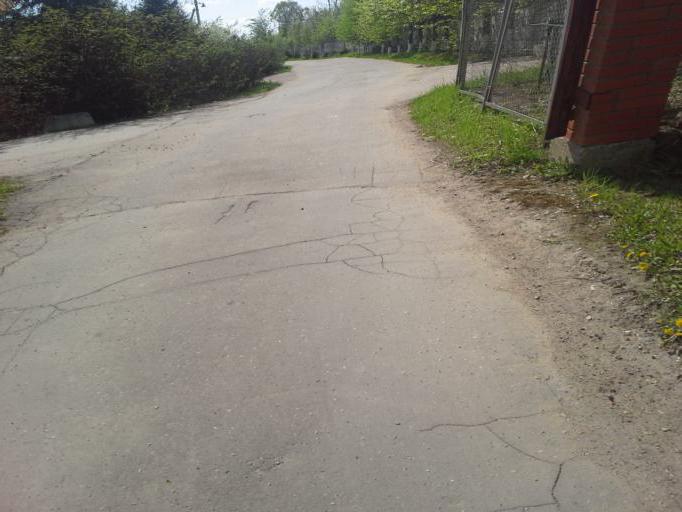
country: RU
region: Moskovskaya
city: Vostryakovo
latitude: 55.6522
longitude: 37.4259
